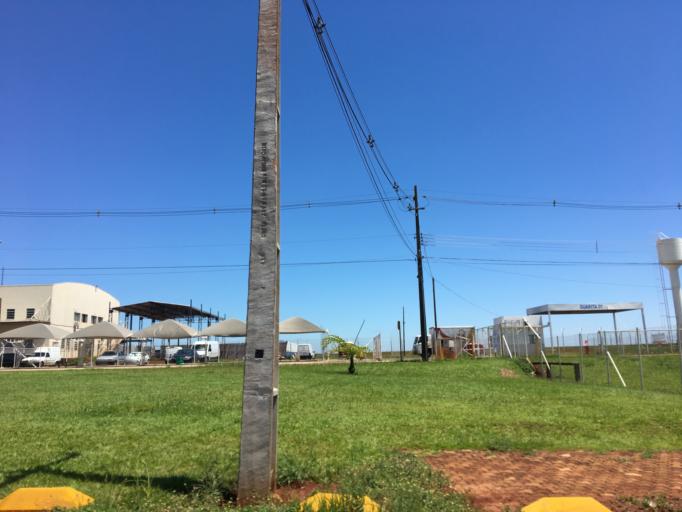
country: BR
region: Parana
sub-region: Paicandu
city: Paicandu
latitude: -23.4798
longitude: -52.0093
